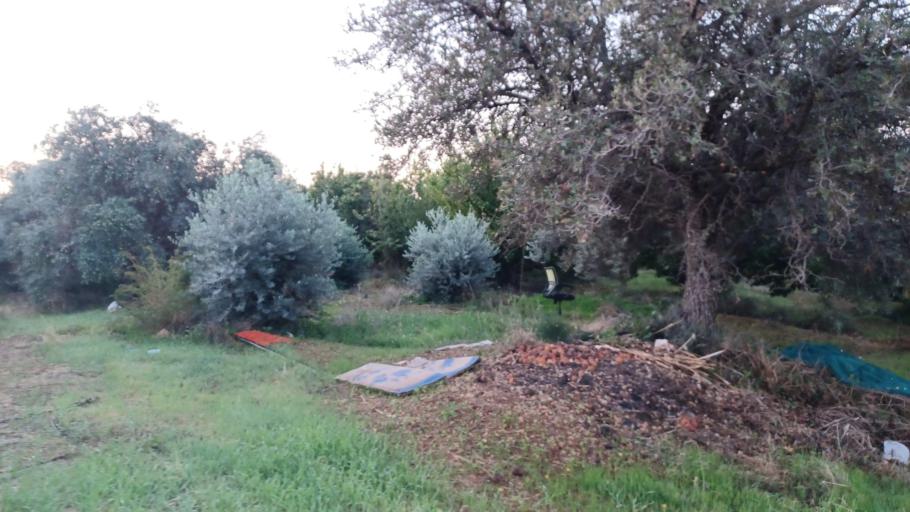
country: CY
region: Pafos
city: Polis
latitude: 35.0004
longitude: 32.4528
